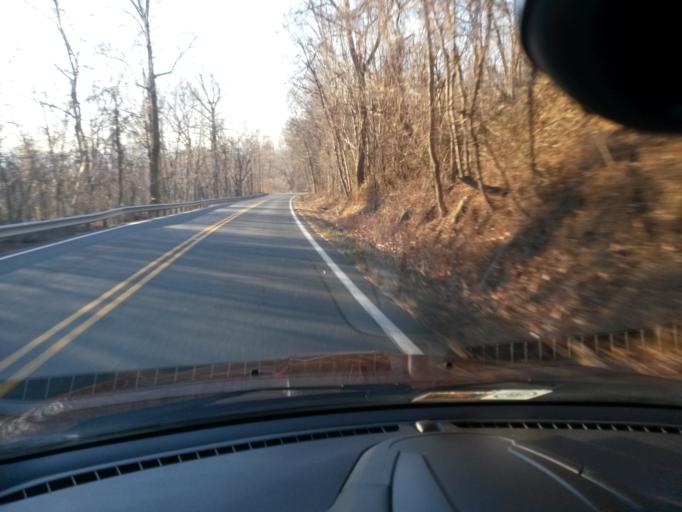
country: US
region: Virginia
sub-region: City of Buena Vista
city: Buena Vista
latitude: 37.7187
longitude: -79.2475
